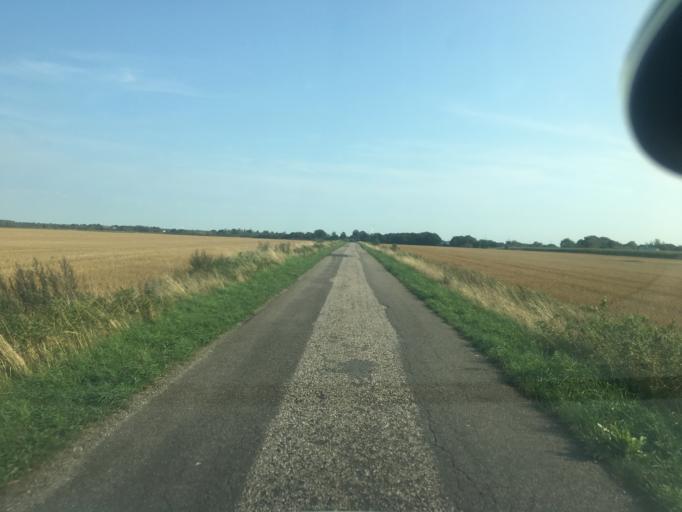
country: DK
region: South Denmark
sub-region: Tonder Kommune
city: Tonder
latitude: 54.9652
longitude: 8.8981
